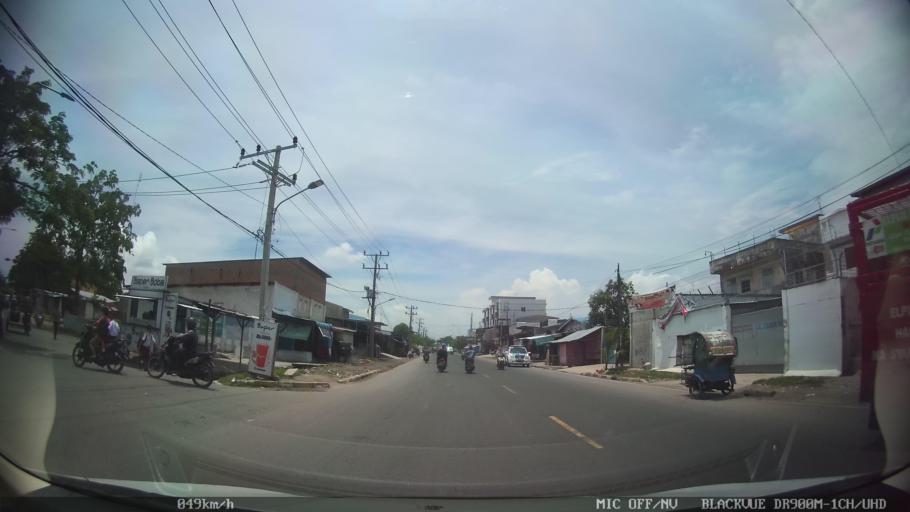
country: ID
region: North Sumatra
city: Belawan
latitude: 3.7754
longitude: 98.6811
